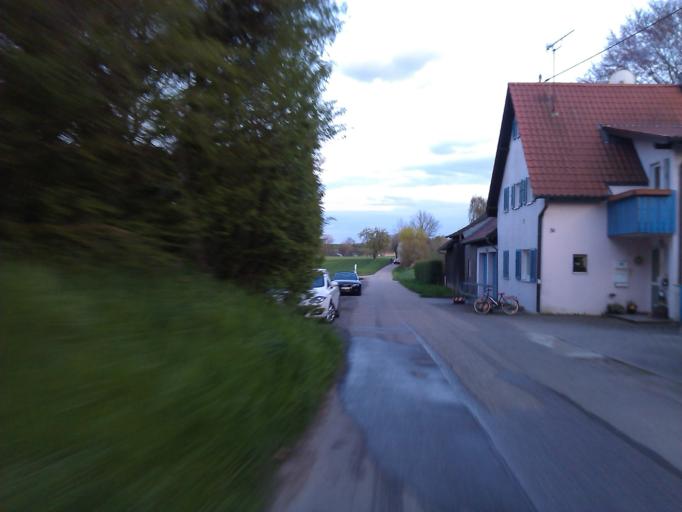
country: DE
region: Baden-Wuerttemberg
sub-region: Regierungsbezirk Stuttgart
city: Bad Wimpfen
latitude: 49.2259
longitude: 9.1670
